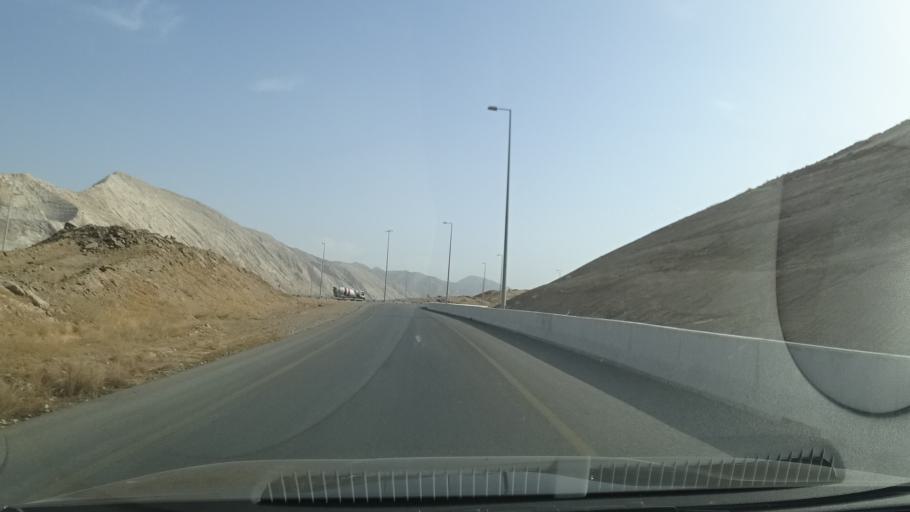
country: OM
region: Muhafazat Masqat
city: Bawshar
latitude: 23.5729
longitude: 58.4231
